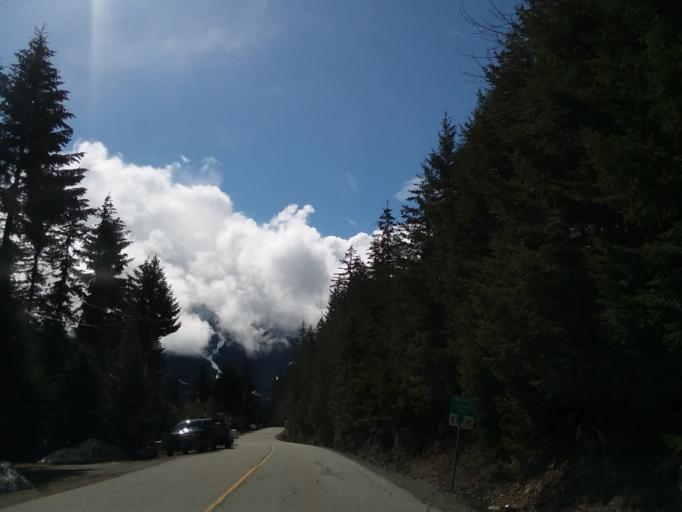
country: CA
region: British Columbia
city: Whistler
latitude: 50.1184
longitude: -122.9864
